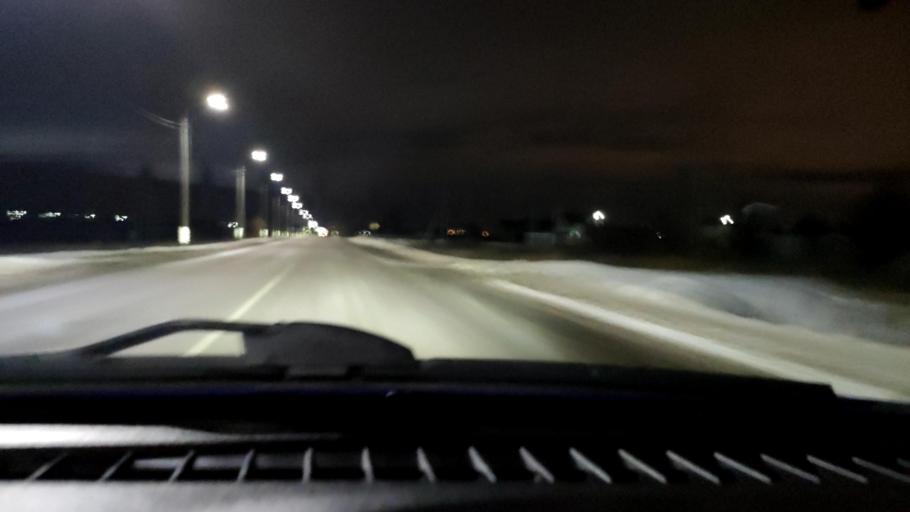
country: RU
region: Voronezj
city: Novaya Usman'
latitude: 51.6645
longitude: 39.4483
